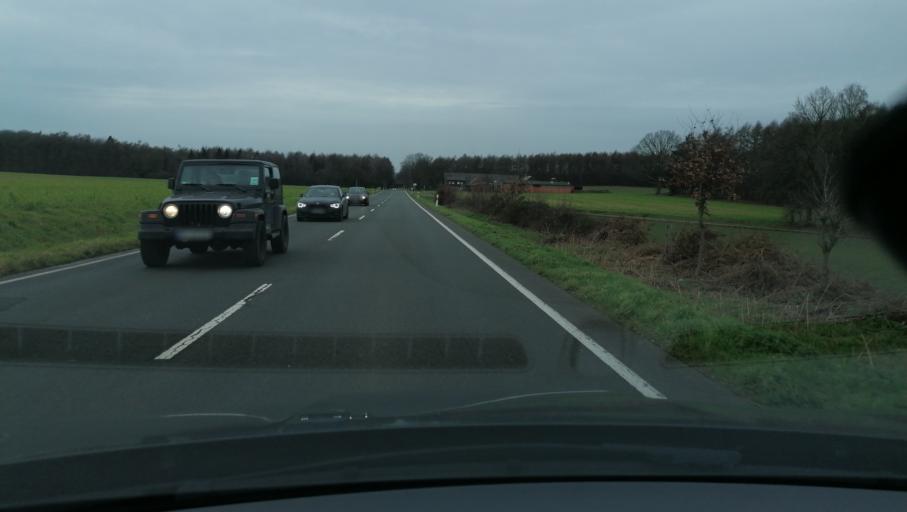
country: DE
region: North Rhine-Westphalia
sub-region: Regierungsbezirk Munster
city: Klein Reken
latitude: 51.7843
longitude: 7.0724
